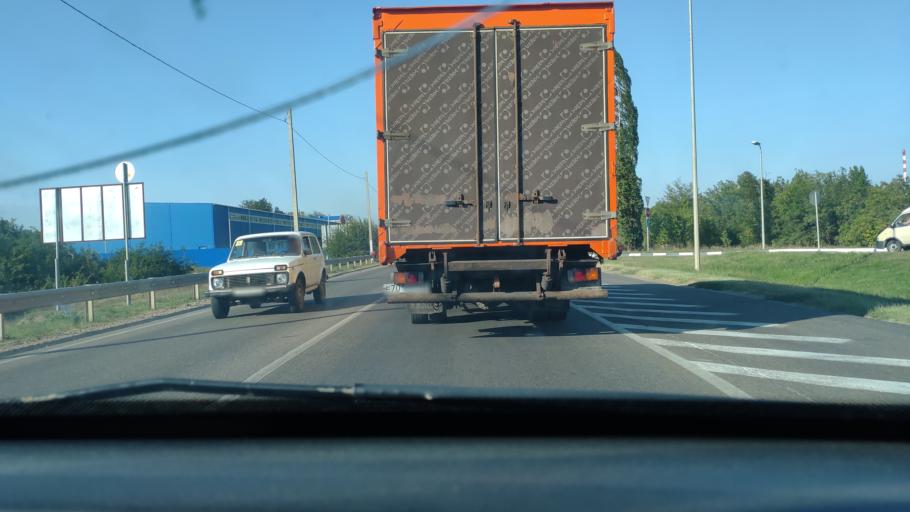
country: RU
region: Krasnodarskiy
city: Novotitarovskaya
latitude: 45.2548
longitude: 38.9965
